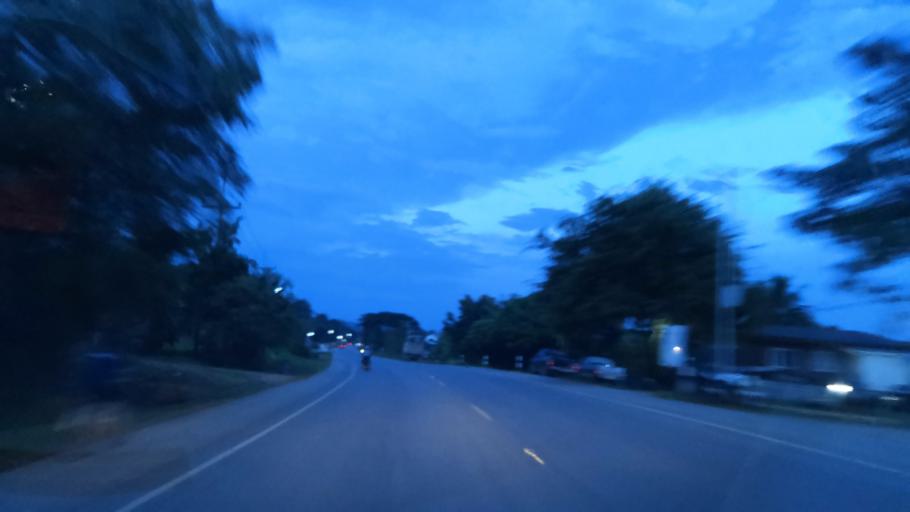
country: TH
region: Chiang Rai
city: Wiang Chiang Rung
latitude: 19.9969
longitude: 100.0390
